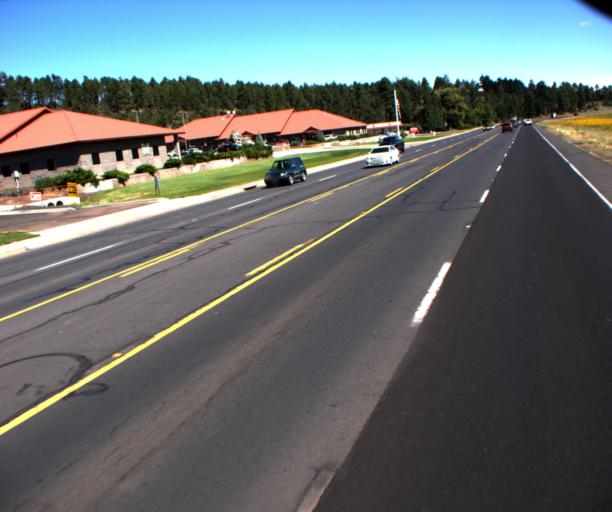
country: US
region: Arizona
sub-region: Navajo County
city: Show Low
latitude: 34.2354
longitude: -110.0265
